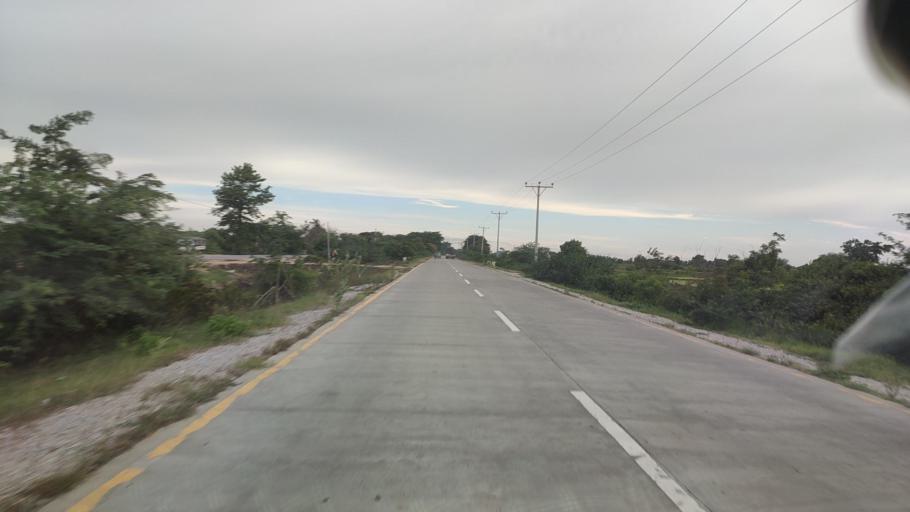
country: MM
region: Mandalay
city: Kyaukse
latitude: 21.3168
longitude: 96.0218
